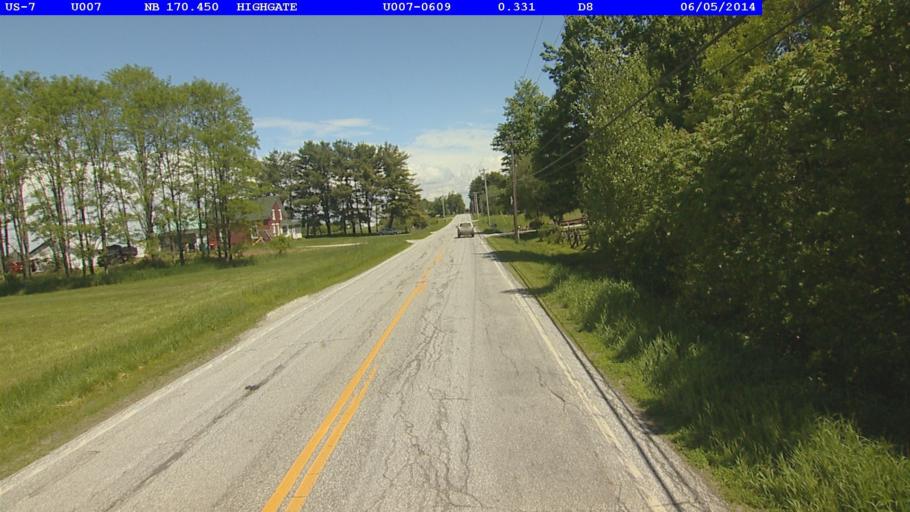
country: US
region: Vermont
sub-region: Franklin County
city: Swanton
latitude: 44.9378
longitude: -73.1180
